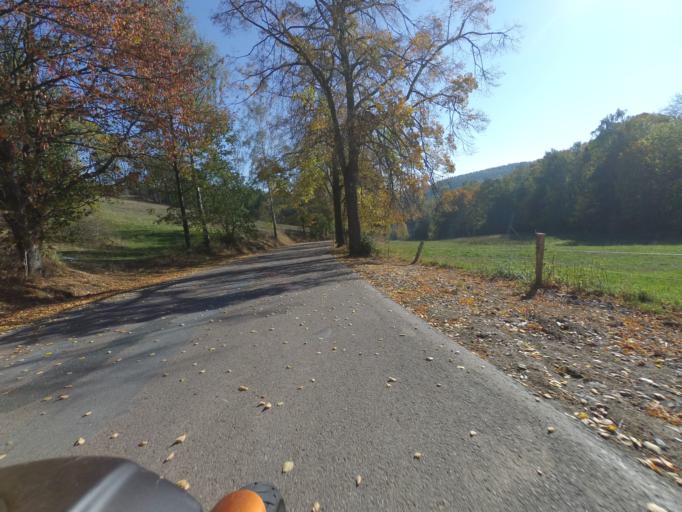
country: DE
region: Saxony
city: Glashutte
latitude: 50.8281
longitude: 13.7564
